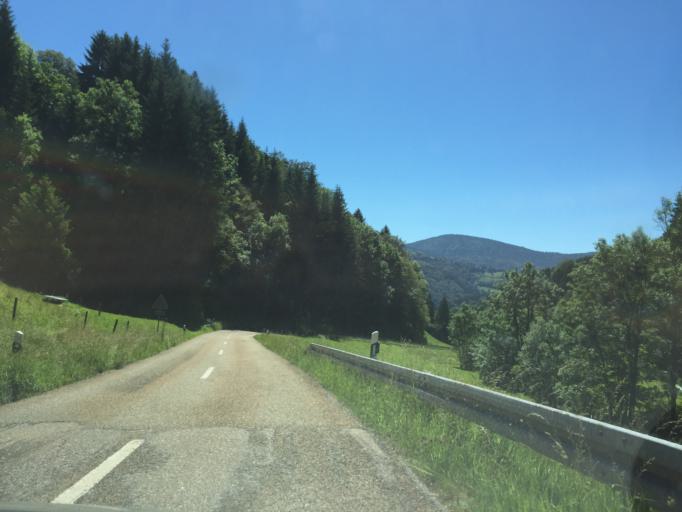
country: DE
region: Baden-Wuerttemberg
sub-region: Freiburg Region
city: Schonenberg
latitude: 47.8107
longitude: 7.8823
